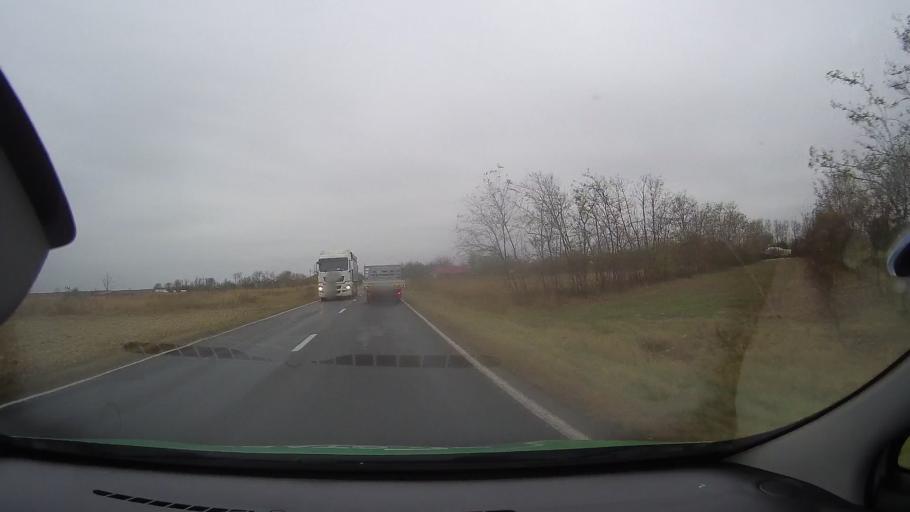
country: RO
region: Ialomita
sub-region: Comuna Scanteia
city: Iazu
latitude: 44.7317
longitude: 27.4289
